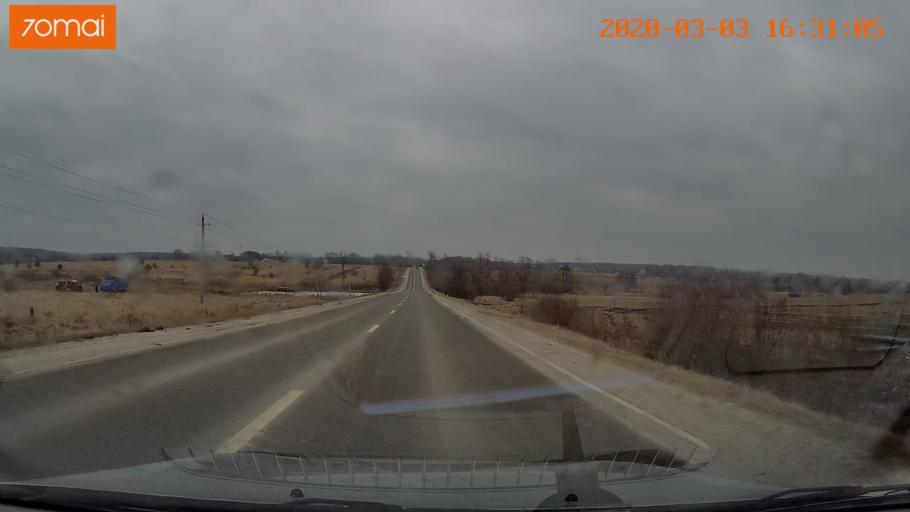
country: RU
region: Moskovskaya
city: Konobeyevo
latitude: 55.4285
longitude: 38.7195
